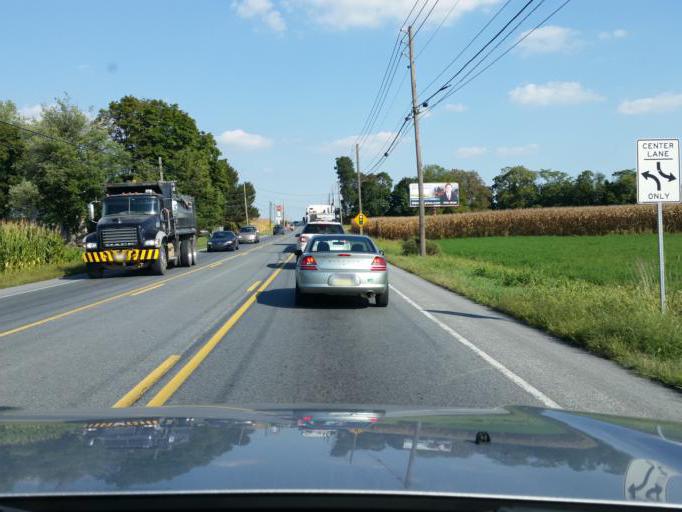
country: US
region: Pennsylvania
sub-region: Lancaster County
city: Gap
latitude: 39.9945
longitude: -76.0368
